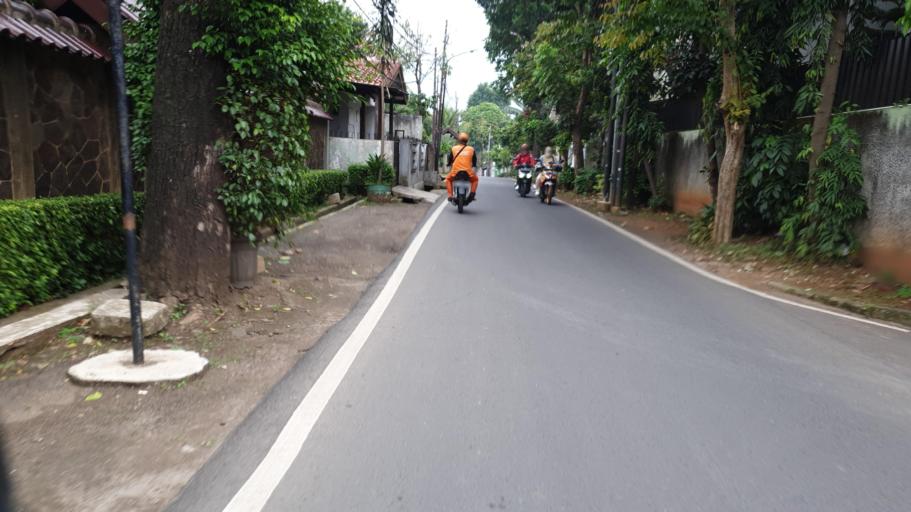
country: ID
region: West Java
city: Depok
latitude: -6.3278
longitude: 106.8223
